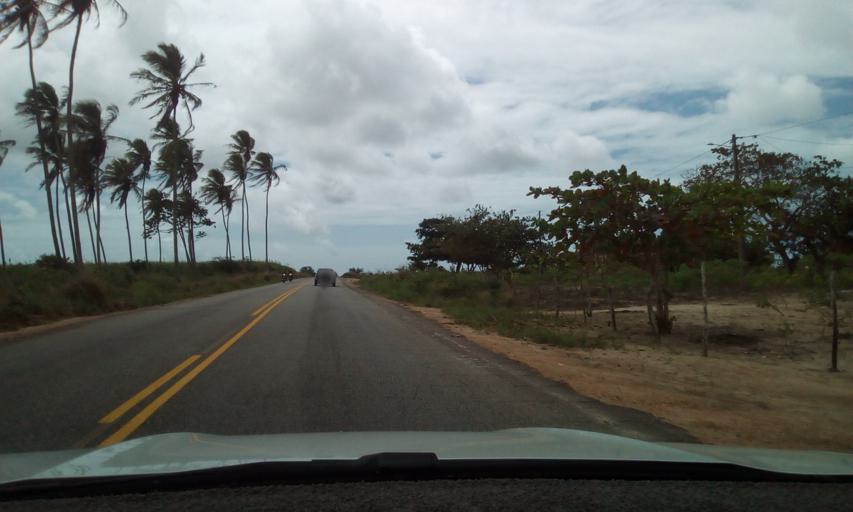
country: BR
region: Paraiba
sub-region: Rio Tinto
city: Rio Tinto
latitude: -6.7686
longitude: -35.0071
